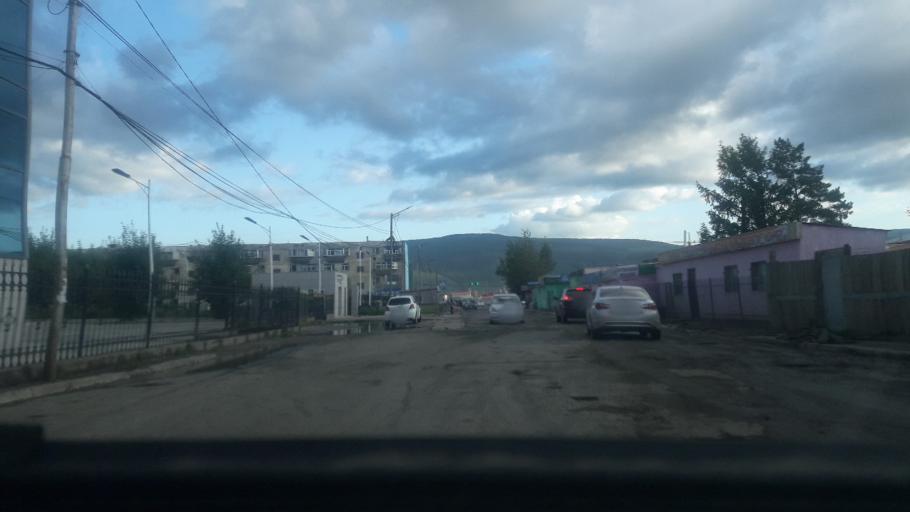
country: MN
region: Ulaanbaatar
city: Ulaanbaatar
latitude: 47.9149
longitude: 106.9947
